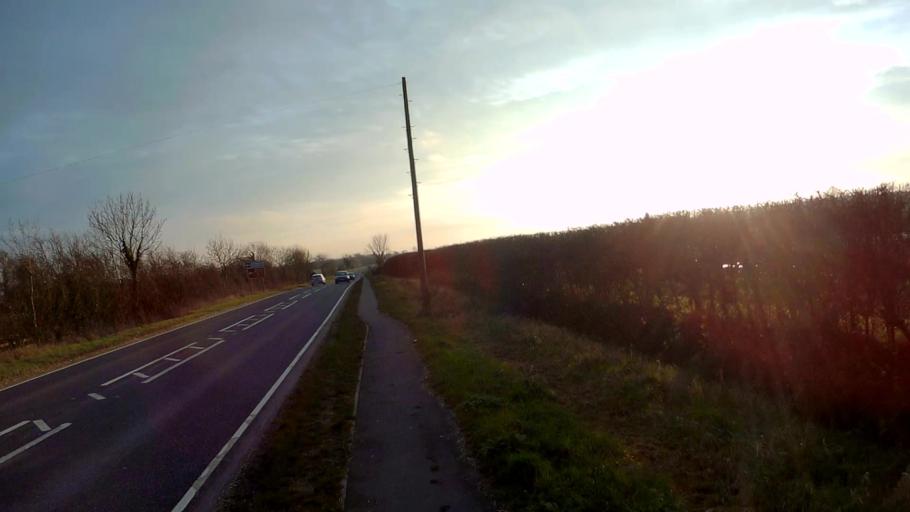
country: GB
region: England
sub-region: Lincolnshire
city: Bourne
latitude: 52.7906
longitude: -0.3764
